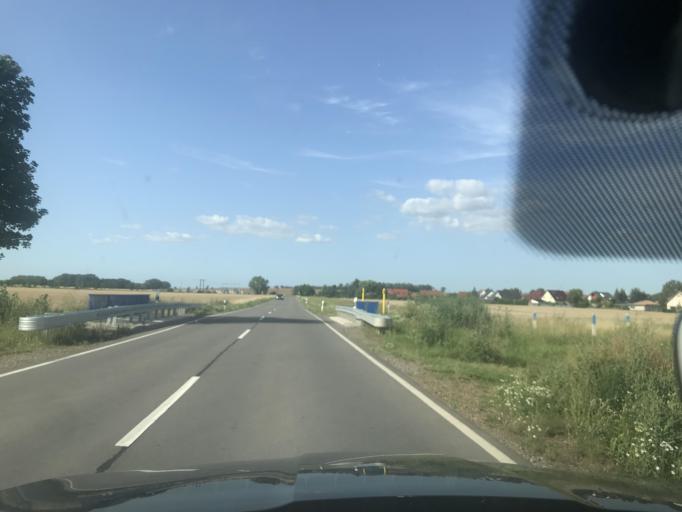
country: DE
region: Saxony-Anhalt
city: Wegeleben
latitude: 51.8861
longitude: 11.1623
